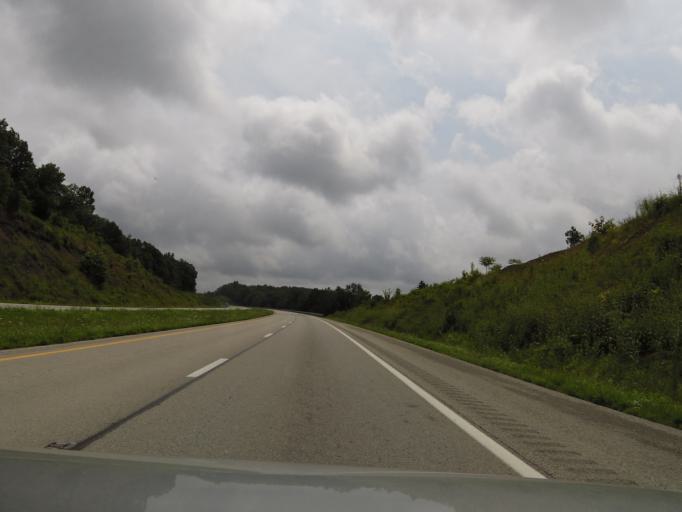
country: US
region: Kentucky
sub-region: Ohio County
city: Oak Grove
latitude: 37.3847
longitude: -86.6599
